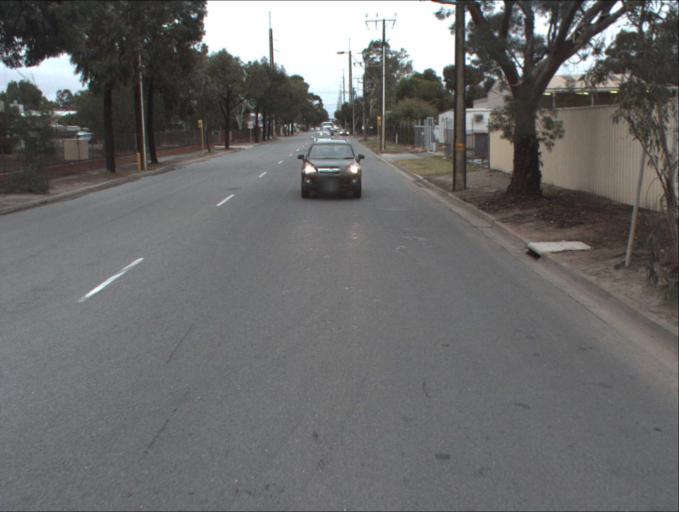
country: AU
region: South Australia
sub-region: Port Adelaide Enfield
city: Enfield
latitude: -34.8338
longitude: 138.5914
